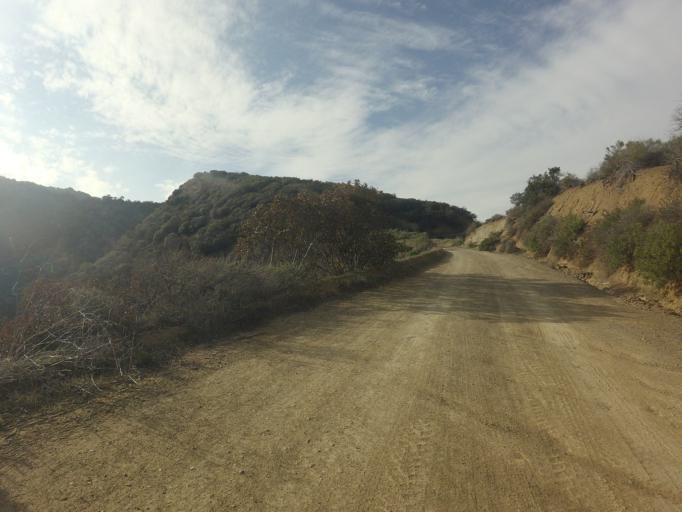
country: US
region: California
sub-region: Riverside County
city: Corona
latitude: 33.8392
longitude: -117.6213
